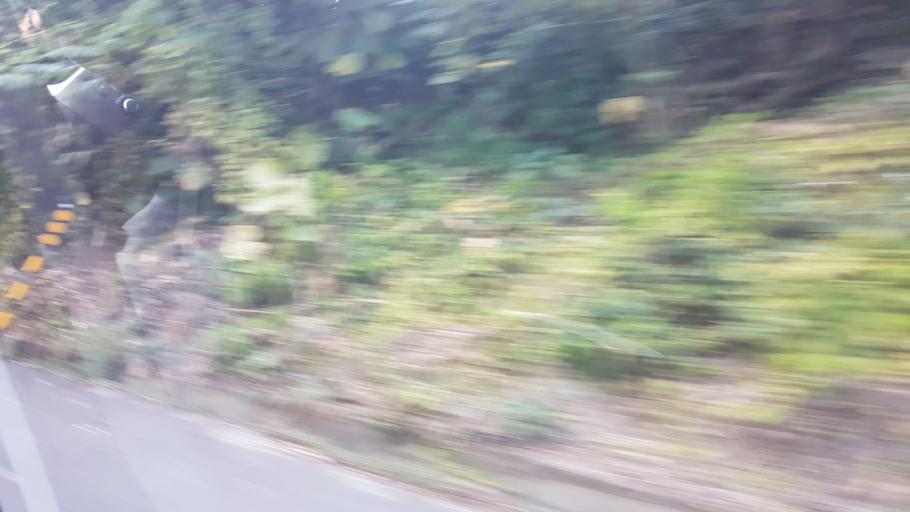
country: TW
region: Taiwan
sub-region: Chiayi
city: Jiayi Shi
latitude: 23.3818
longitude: 120.4392
